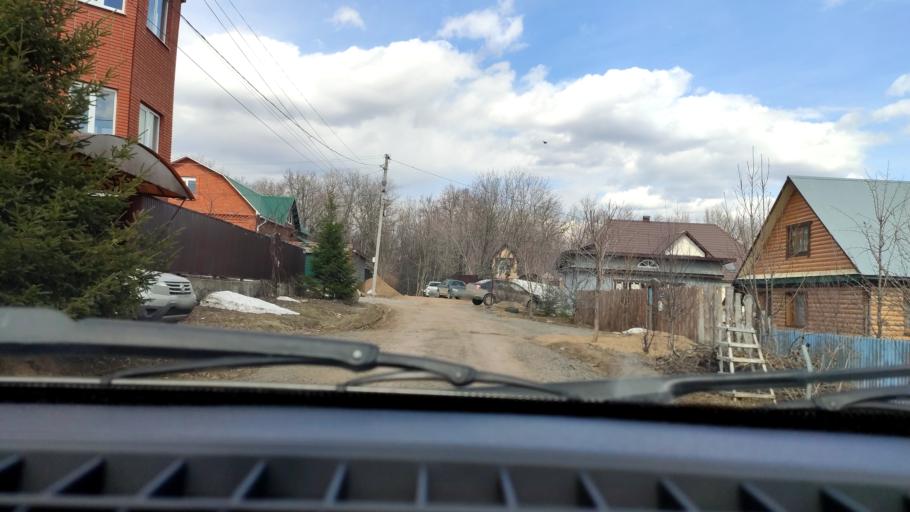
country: RU
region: Bashkortostan
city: Mikhaylovka
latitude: 54.8216
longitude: 55.8956
